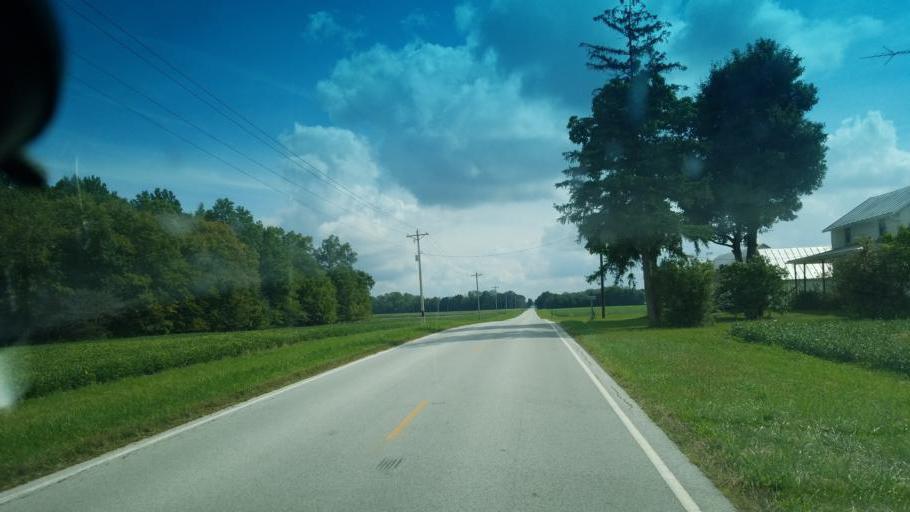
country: US
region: Ohio
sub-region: Wyandot County
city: Carey
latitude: 40.9635
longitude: -83.3422
